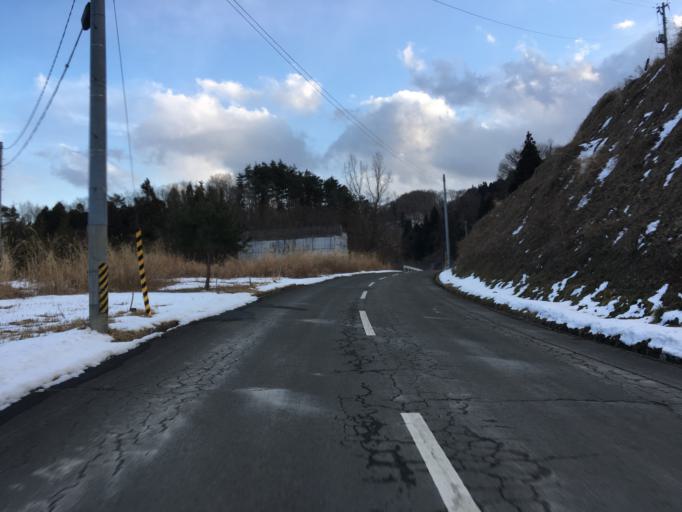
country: JP
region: Fukushima
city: Fukushima-shi
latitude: 37.6415
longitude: 140.5871
